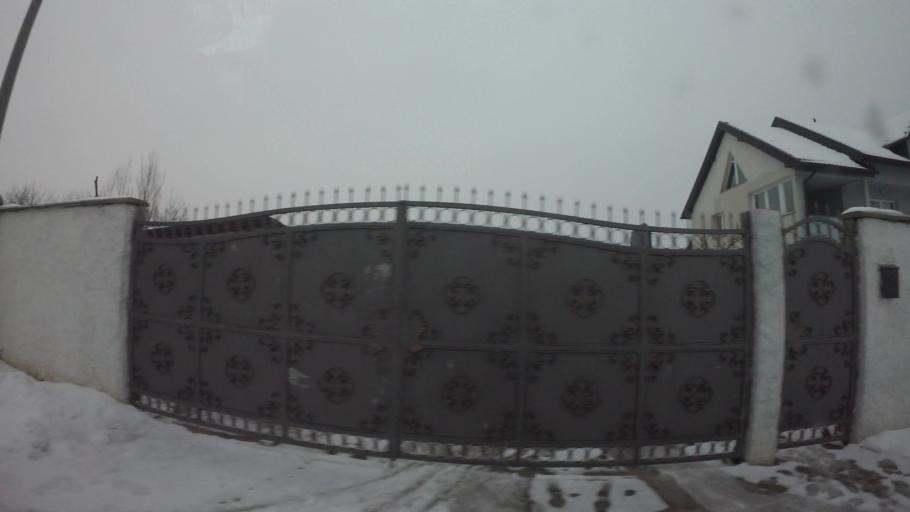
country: BA
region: Federation of Bosnia and Herzegovina
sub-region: Kanton Sarajevo
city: Sarajevo
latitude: 43.8446
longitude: 18.2972
